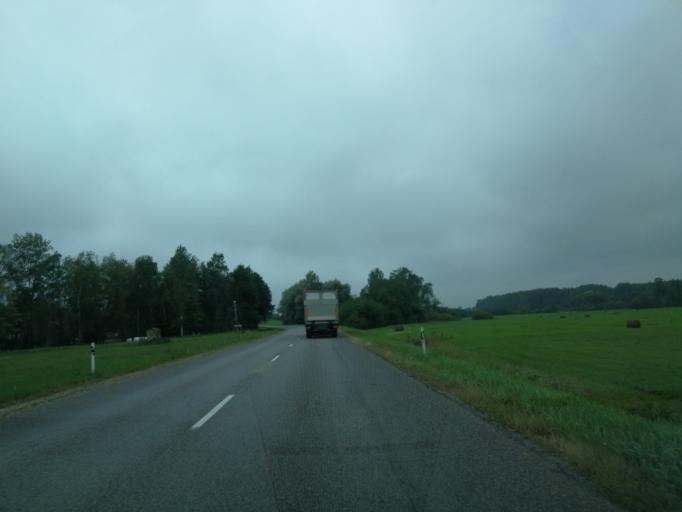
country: LV
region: Livani
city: Livani
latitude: 56.3478
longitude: 26.3073
